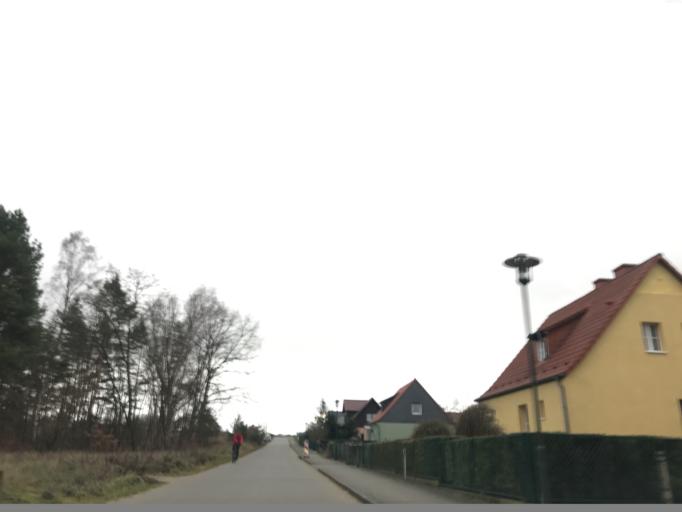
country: DE
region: Brandenburg
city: Rheinsberg
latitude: 53.0922
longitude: 12.8903
